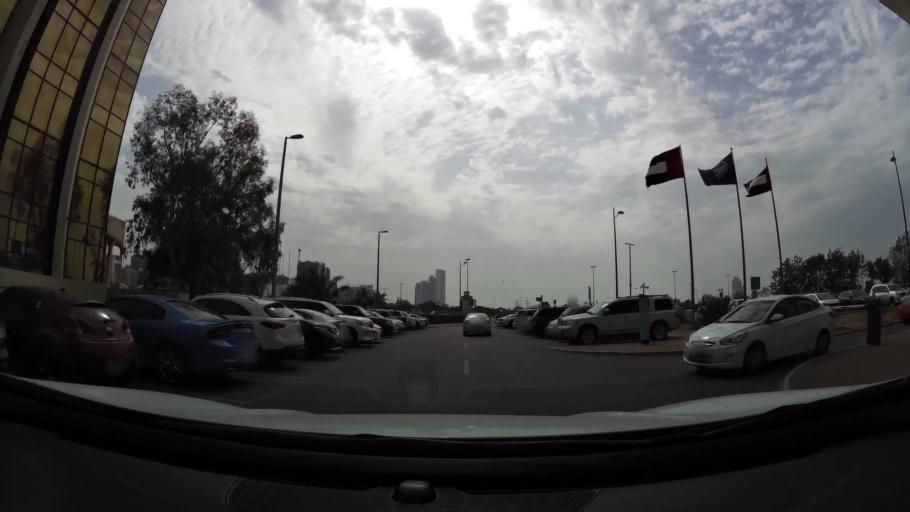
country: AE
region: Abu Dhabi
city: Abu Dhabi
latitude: 24.4817
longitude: 54.3499
